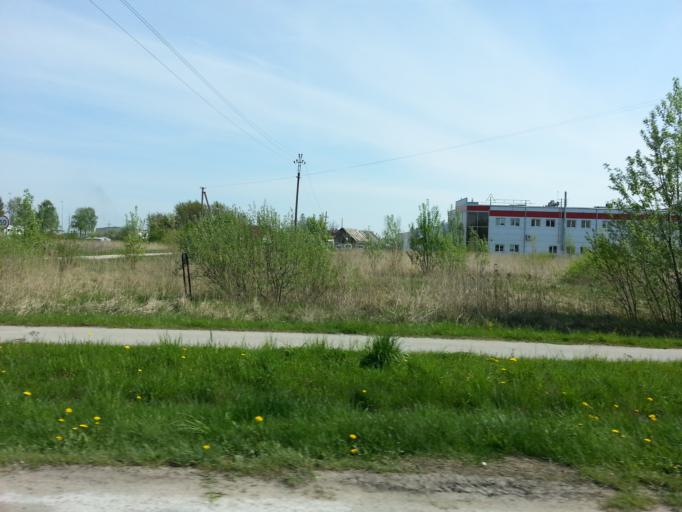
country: LT
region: Panevezys
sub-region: Panevezys City
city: Panevezys
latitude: 55.7592
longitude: 24.3060
